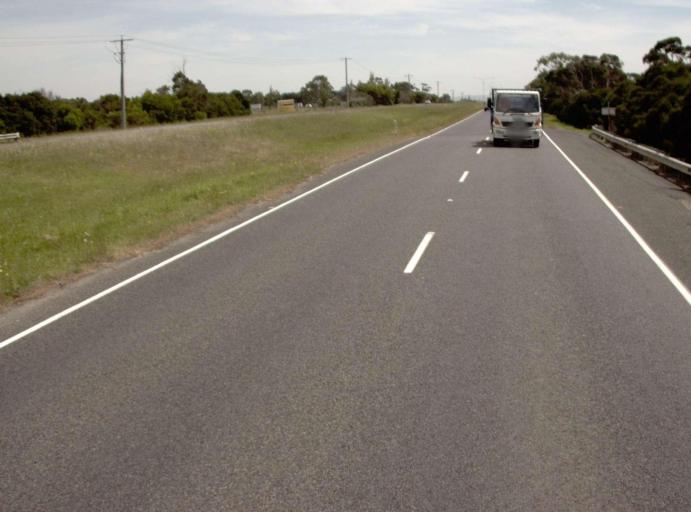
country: AU
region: Victoria
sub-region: Casey
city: Cranbourne South
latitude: -38.1179
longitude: 145.2315
